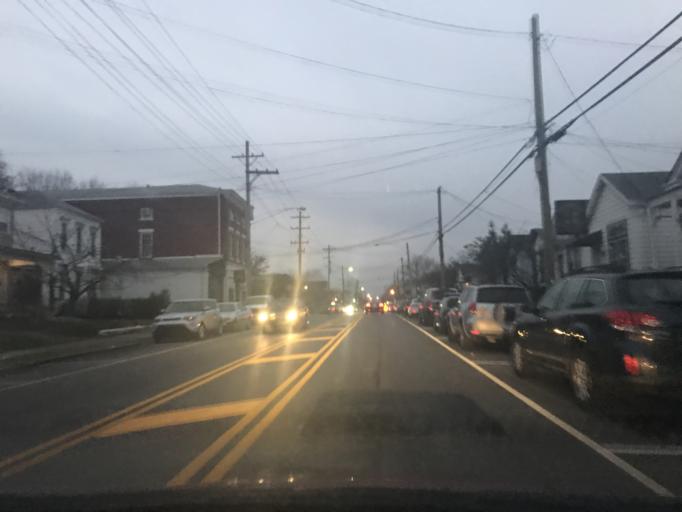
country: US
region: Kentucky
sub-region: Jefferson County
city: Audubon Park
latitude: 38.2287
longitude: -85.7378
